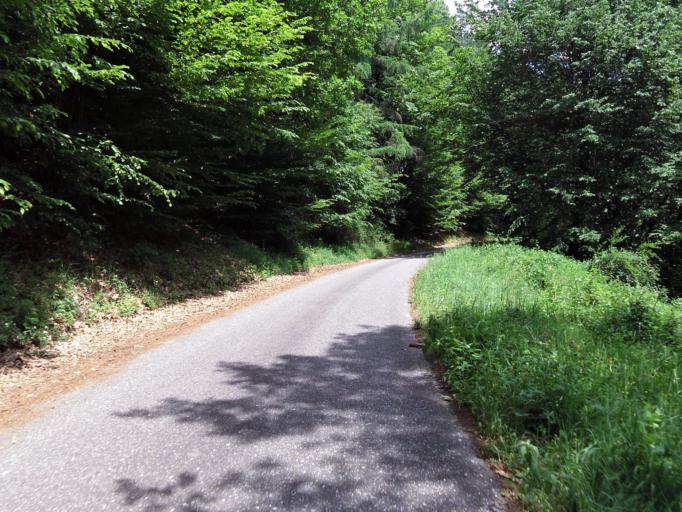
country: DE
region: Rheinland-Pfalz
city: Frankenstein
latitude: 49.4323
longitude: 7.9709
